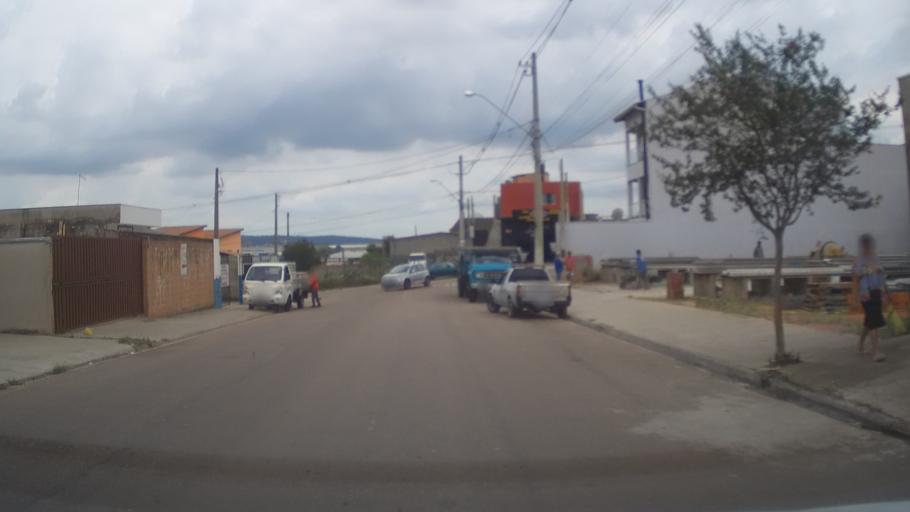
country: BR
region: Sao Paulo
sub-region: Itupeva
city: Itupeva
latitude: -23.1497
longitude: -47.0067
